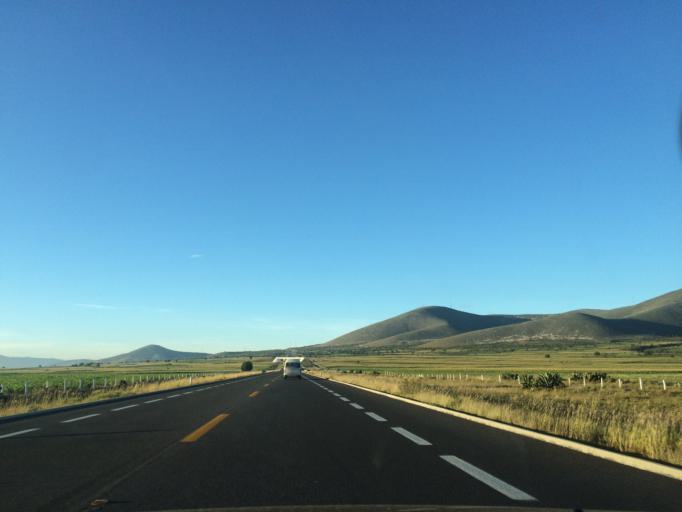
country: MX
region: Puebla
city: Morelos Canada
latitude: 18.7502
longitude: -97.4799
